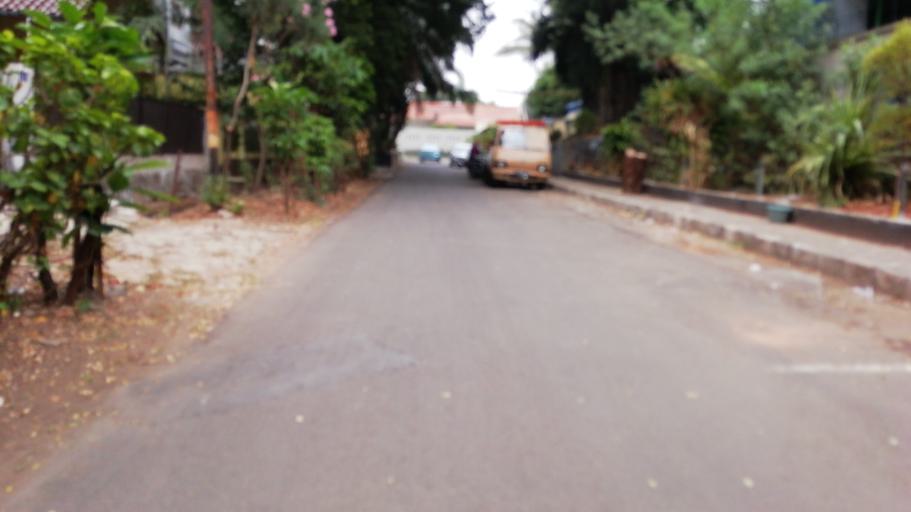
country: ID
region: Jakarta Raya
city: Jakarta
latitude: -6.2550
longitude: 106.7987
